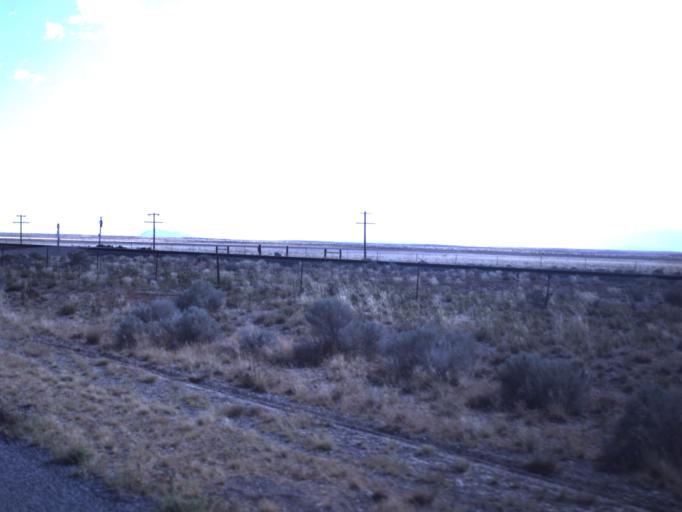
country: US
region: Utah
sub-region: Millard County
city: Fillmore
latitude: 38.9188
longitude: -112.8124
